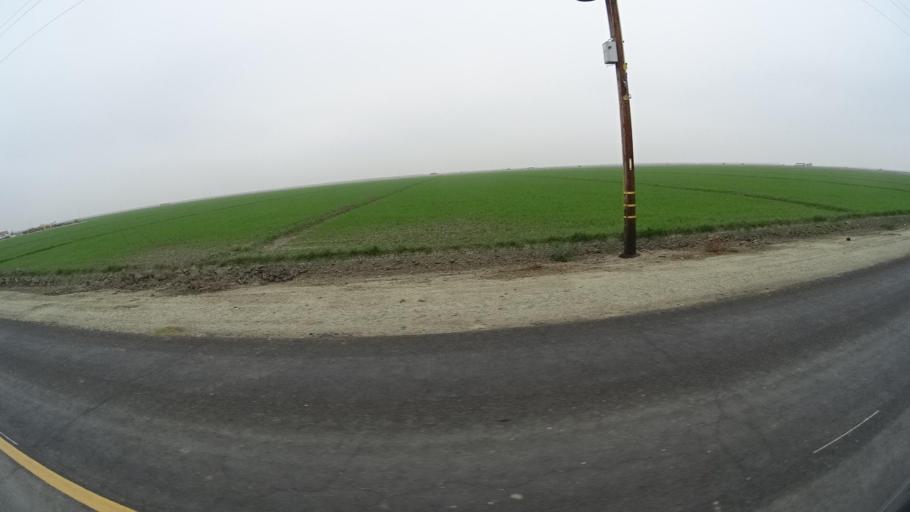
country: US
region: California
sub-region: Kern County
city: Greenfield
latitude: 35.1800
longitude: -119.1406
